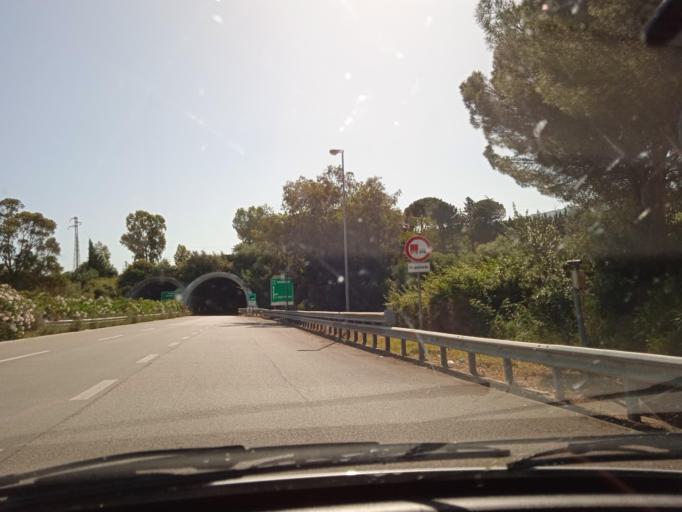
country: IT
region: Sicily
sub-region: Messina
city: Acquedolci
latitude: 38.0541
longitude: 14.6036
